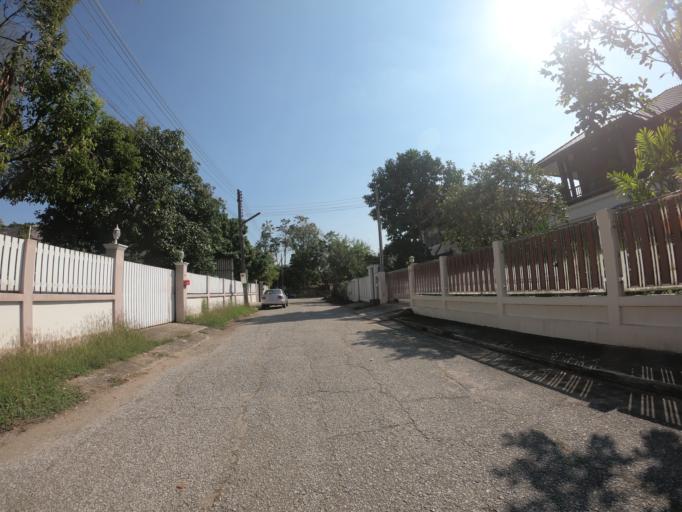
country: TH
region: Chiang Mai
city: Chiang Mai
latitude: 18.8065
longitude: 99.0067
